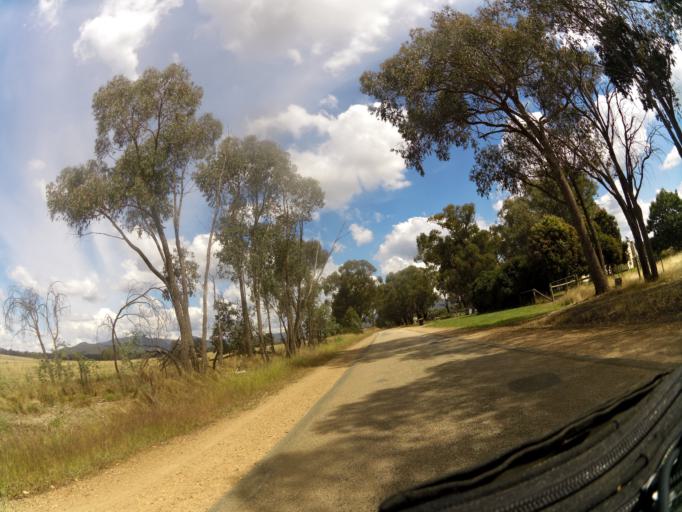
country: AU
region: Victoria
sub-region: Benalla
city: Benalla
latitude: -36.7530
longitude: 145.9801
